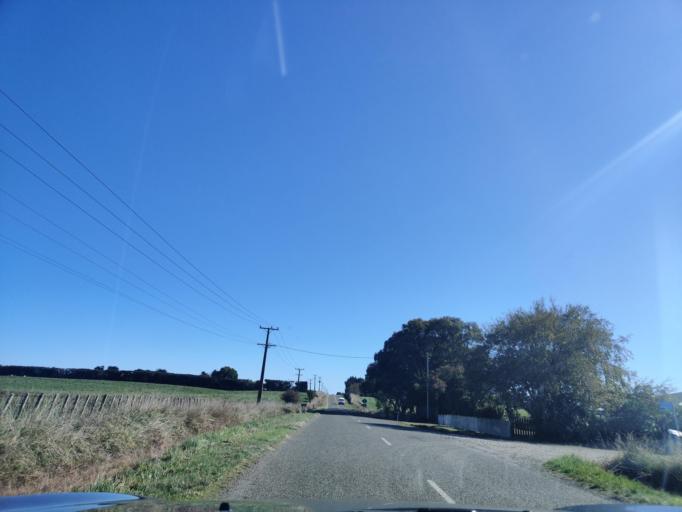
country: NZ
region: Manawatu-Wanganui
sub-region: Palmerston North City
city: Palmerston North
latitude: -40.2340
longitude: 175.6569
